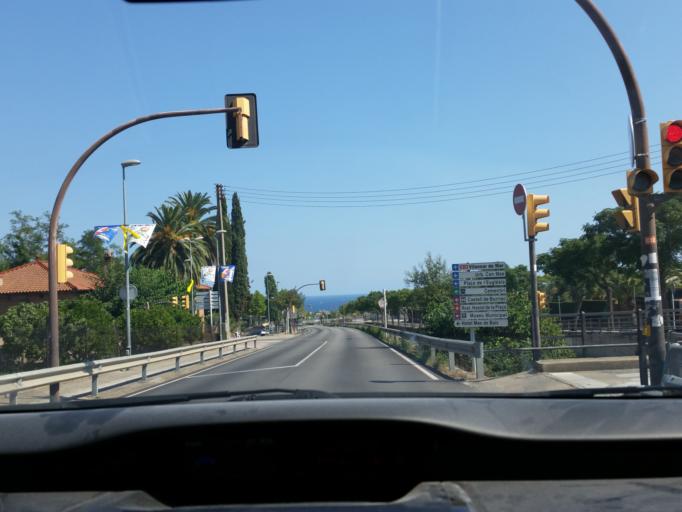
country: ES
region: Catalonia
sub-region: Provincia de Barcelona
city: Cabrils
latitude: 41.5234
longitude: 2.3686
